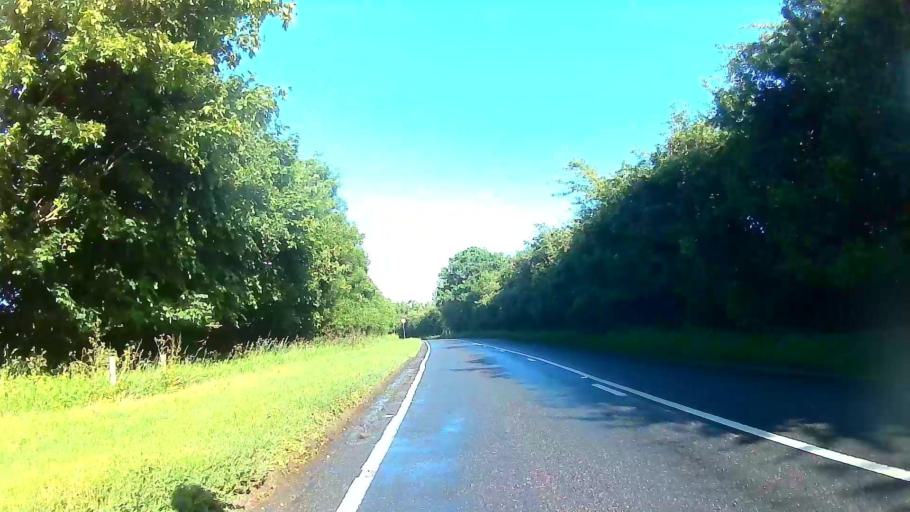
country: GB
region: England
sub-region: Essex
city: Ingatestone
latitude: 51.7138
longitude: 0.3830
